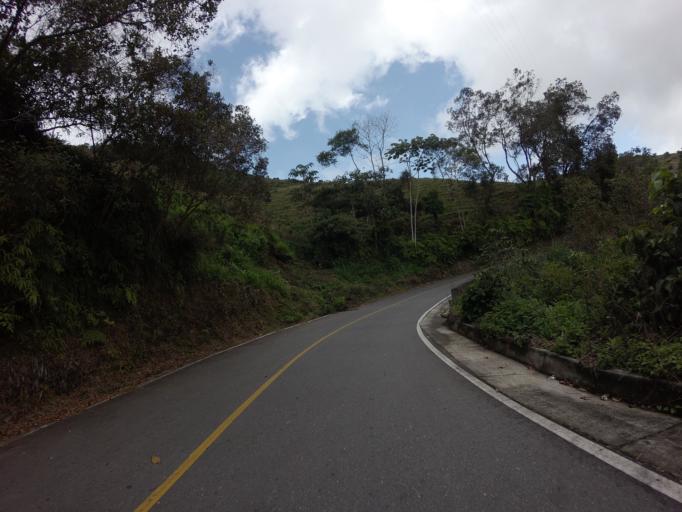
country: CO
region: Caldas
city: Marquetalia
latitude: 5.2752
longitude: -75.1059
